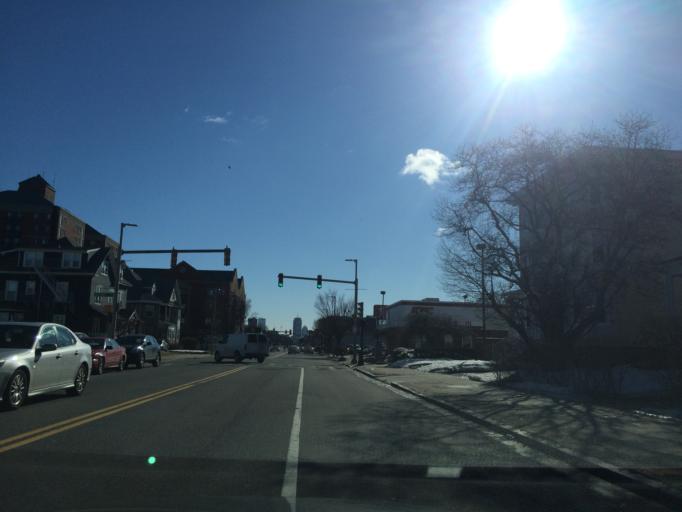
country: US
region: Massachusetts
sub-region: Norfolk County
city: Brookline
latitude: 42.3538
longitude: -71.1397
